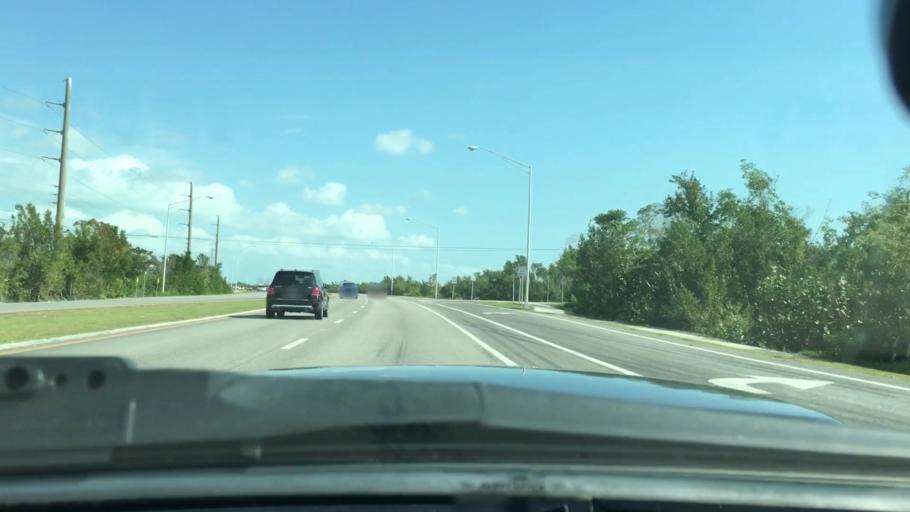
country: US
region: Florida
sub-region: Monroe County
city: Stock Island
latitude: 24.5789
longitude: -81.7082
